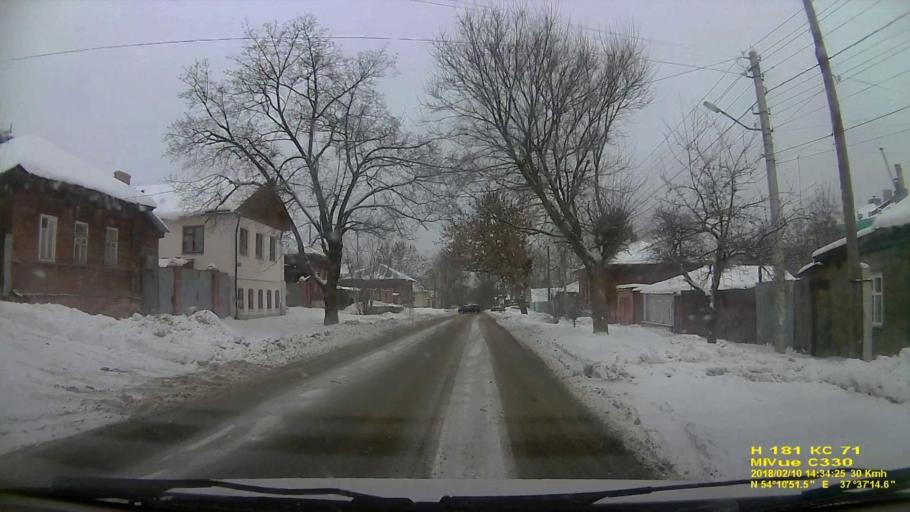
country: RU
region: Tula
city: Tula
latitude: 54.1810
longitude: 37.6207
